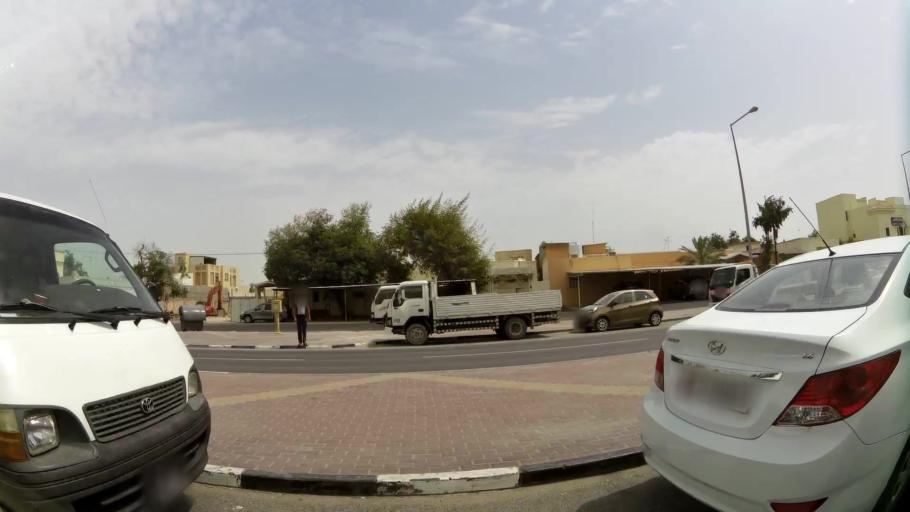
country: QA
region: Baladiyat ar Rayyan
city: Ar Rayyan
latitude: 25.3184
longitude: 51.4774
